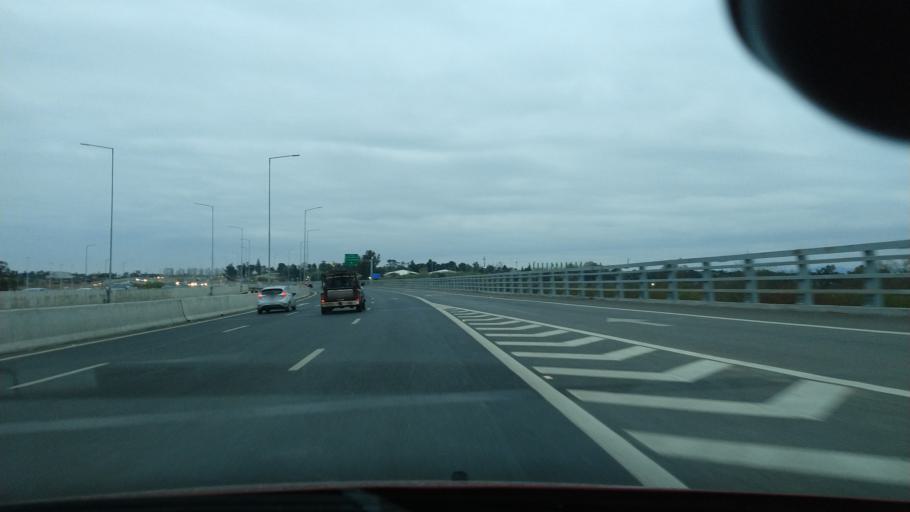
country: AR
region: Cordoba
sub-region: Departamento de Capital
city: Cordoba
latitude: -31.3653
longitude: -64.2488
